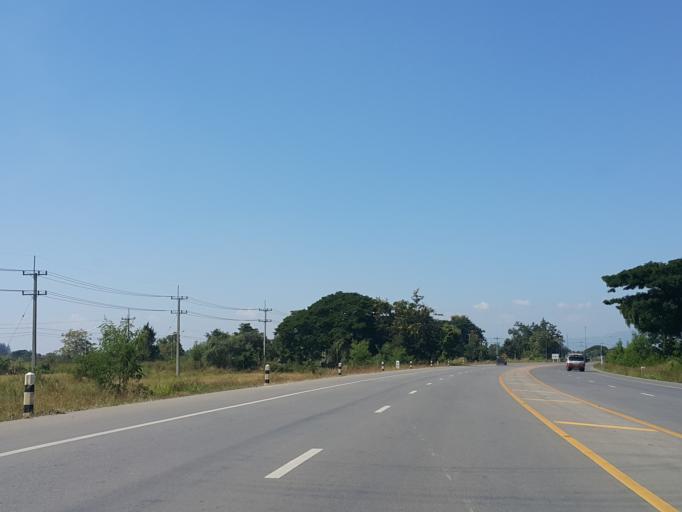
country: TH
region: Chiang Mai
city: San Kamphaeng
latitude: 18.7110
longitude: 99.1282
